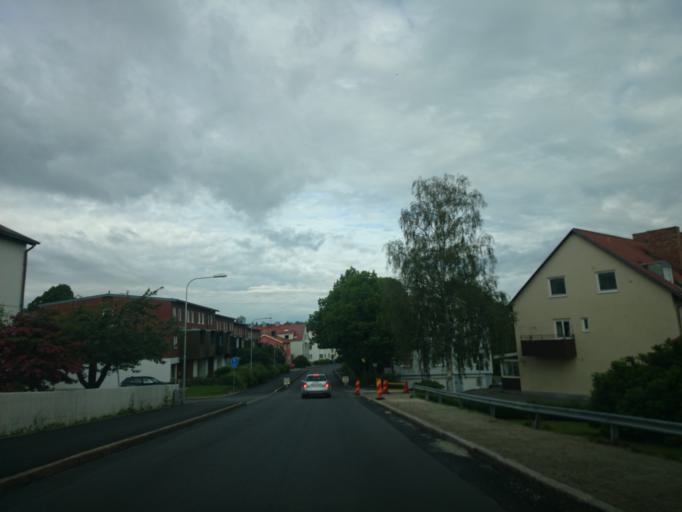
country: SE
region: Vaesternorrland
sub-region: Sundsvalls Kommun
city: Sundsvall
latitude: 62.3809
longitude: 17.3273
